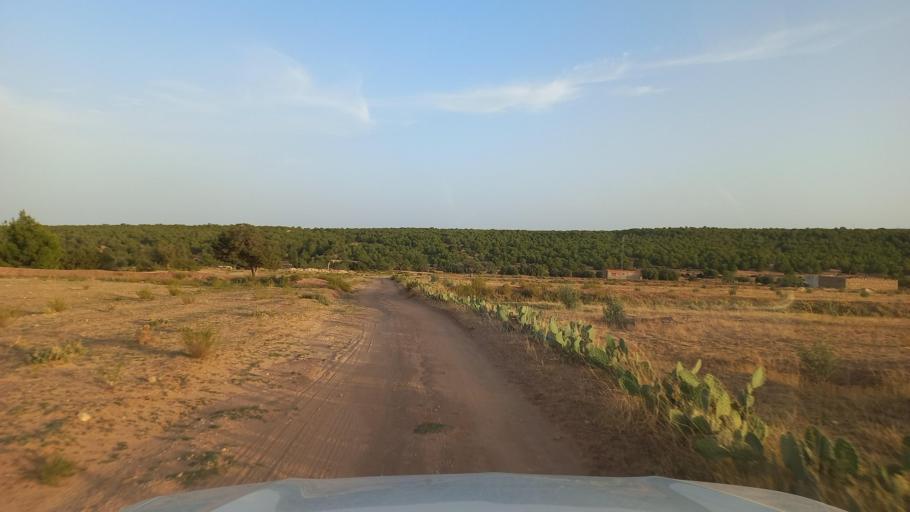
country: TN
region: Al Qasrayn
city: Sbiba
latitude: 35.4103
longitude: 8.9138
